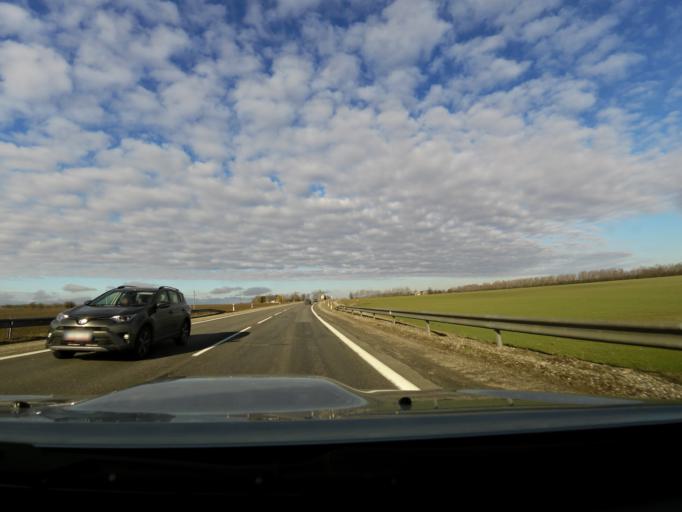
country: LT
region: Panevezys
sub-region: Panevezys City
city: Panevezys
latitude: 55.7354
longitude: 24.2126
